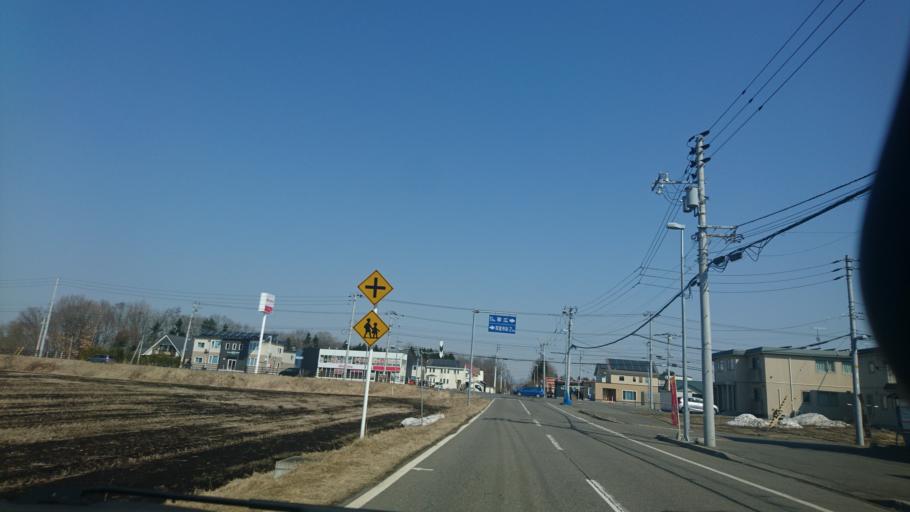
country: JP
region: Hokkaido
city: Obihiro
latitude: 42.9116
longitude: 143.0702
